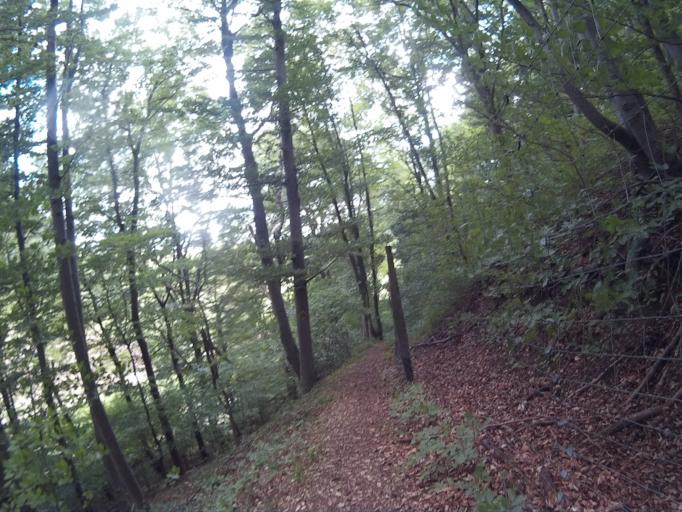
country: HU
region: Veszprem
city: Herend
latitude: 47.1052
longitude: 17.7763
